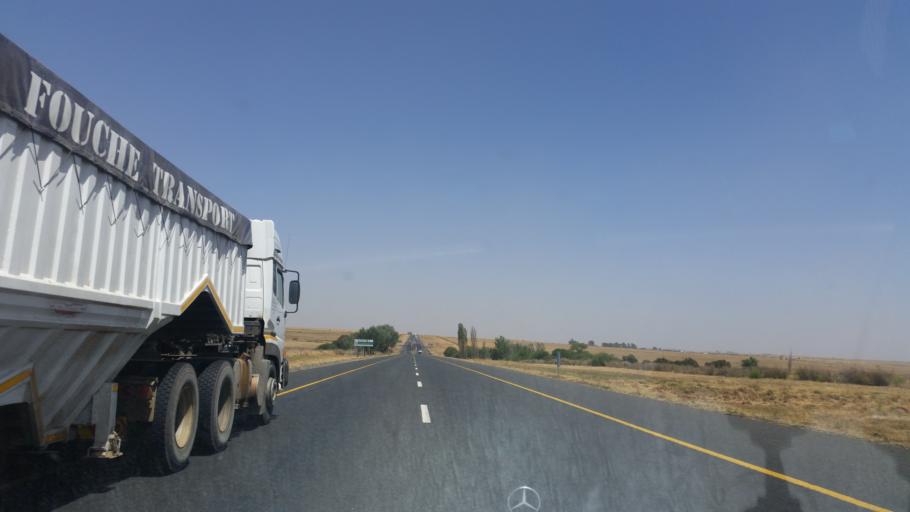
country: ZA
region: Orange Free State
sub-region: Lejweleputswa District Municipality
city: Brandfort
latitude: -28.7312
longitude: 26.7618
